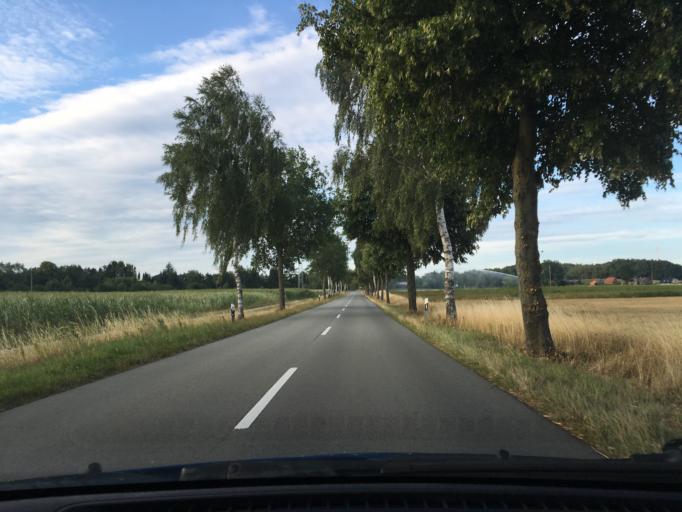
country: DE
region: Lower Saxony
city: Thomasburg
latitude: 53.1900
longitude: 10.6313
